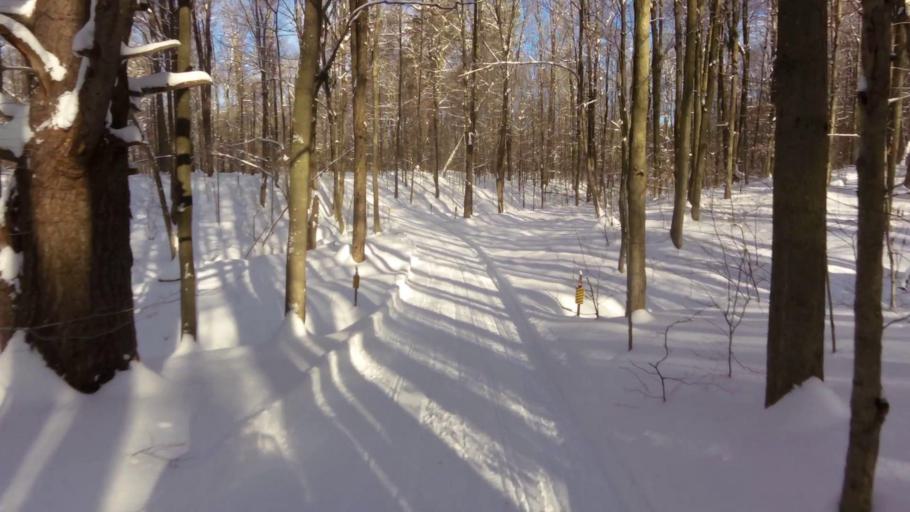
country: US
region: New York
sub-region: Chautauqua County
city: Falconer
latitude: 42.2594
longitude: -79.1446
